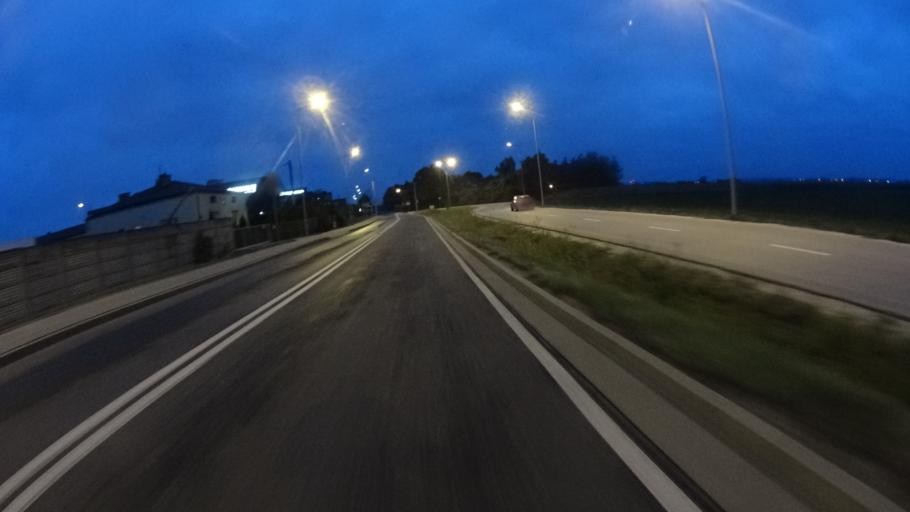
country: PL
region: Masovian Voivodeship
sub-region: Powiat warszawski zachodni
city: Babice
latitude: 52.2285
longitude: 20.8744
